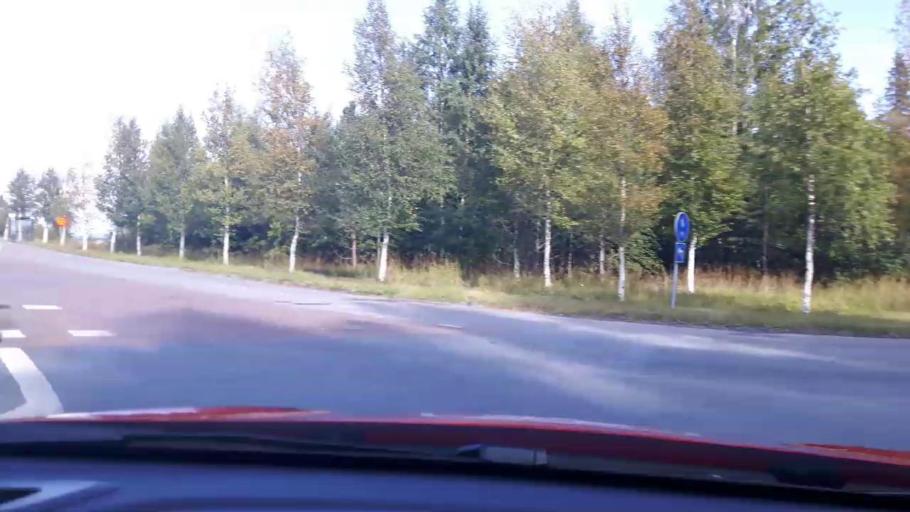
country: SE
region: Jaemtland
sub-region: OEstersunds Kommun
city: Ostersund
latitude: 63.1516
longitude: 14.5909
